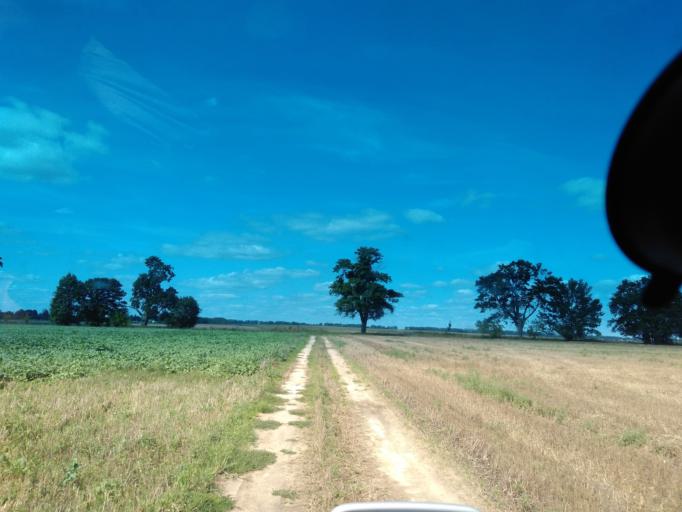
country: BY
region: Minsk
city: Stan'kava
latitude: 53.6333
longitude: 27.3257
